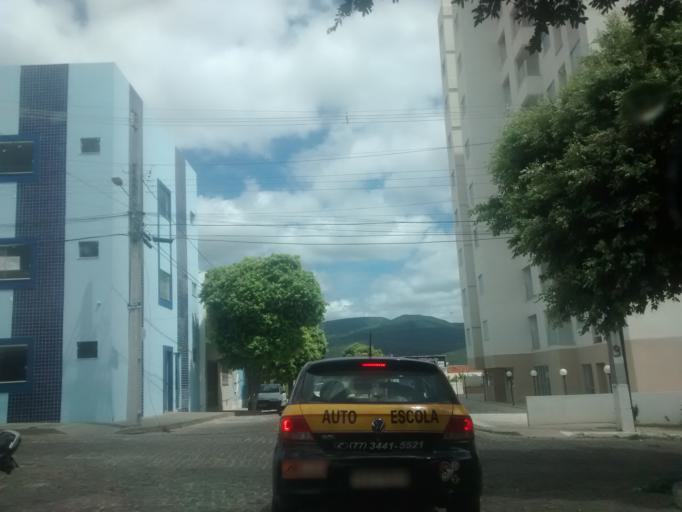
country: BR
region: Bahia
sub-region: Brumado
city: Brumado
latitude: -14.2026
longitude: -41.6705
